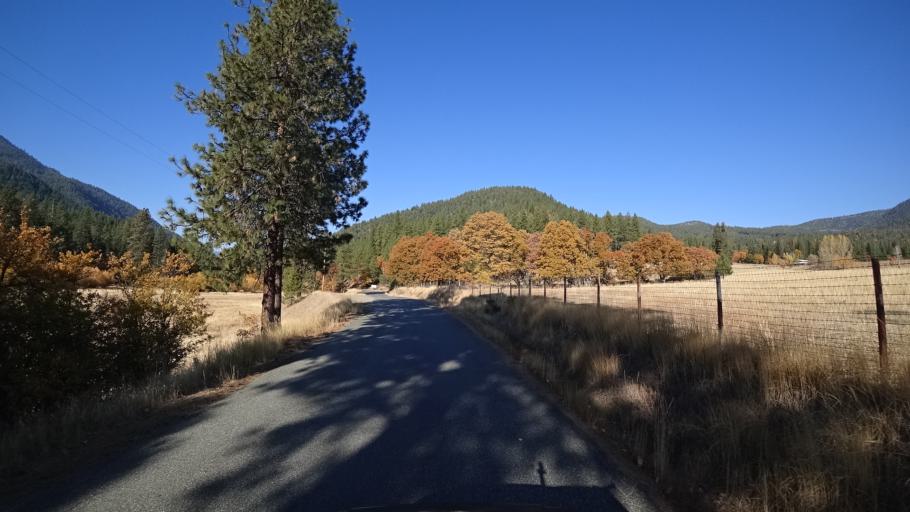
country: US
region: California
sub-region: Siskiyou County
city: Yreka
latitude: 41.6411
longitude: -122.9946
